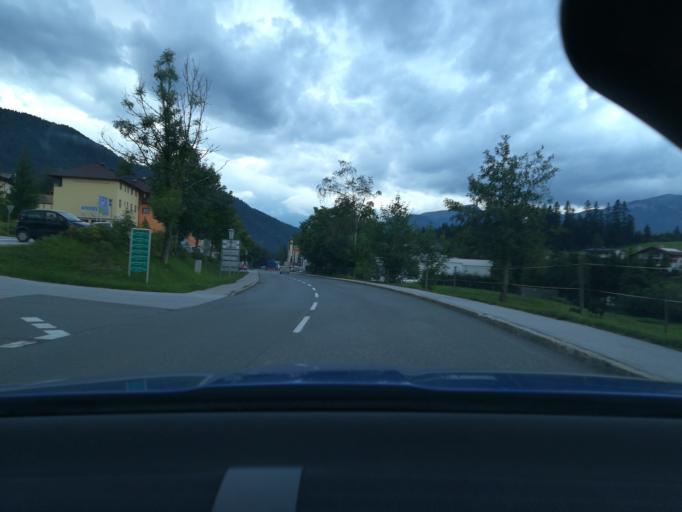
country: AT
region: Salzburg
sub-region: Politischer Bezirk Hallein
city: Abtenau
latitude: 47.5670
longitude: 13.3400
